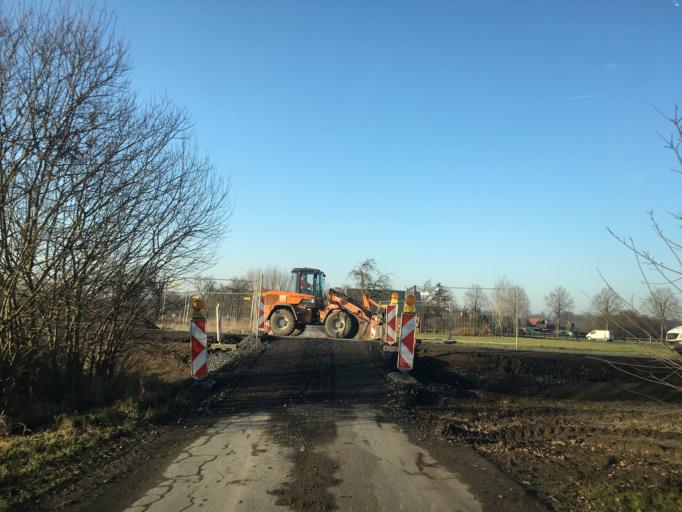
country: DE
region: North Rhine-Westphalia
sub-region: Regierungsbezirk Munster
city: Nordwalde
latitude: 52.0808
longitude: 7.4939
